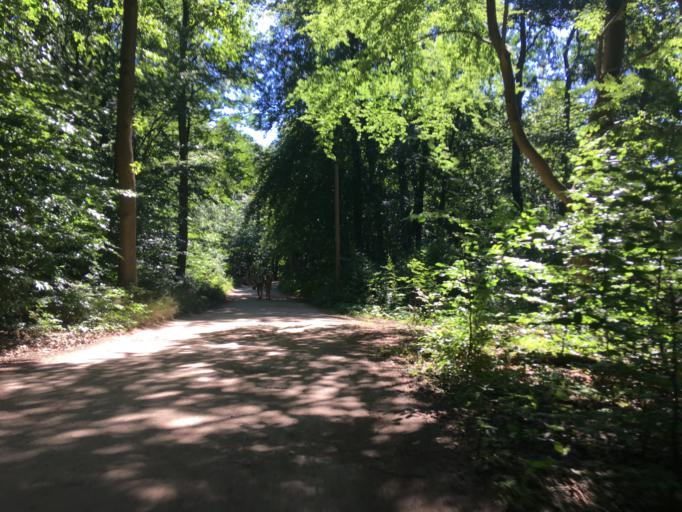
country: DE
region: Brandenburg
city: Grosswoltersdorf
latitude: 53.1512
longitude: 13.0414
